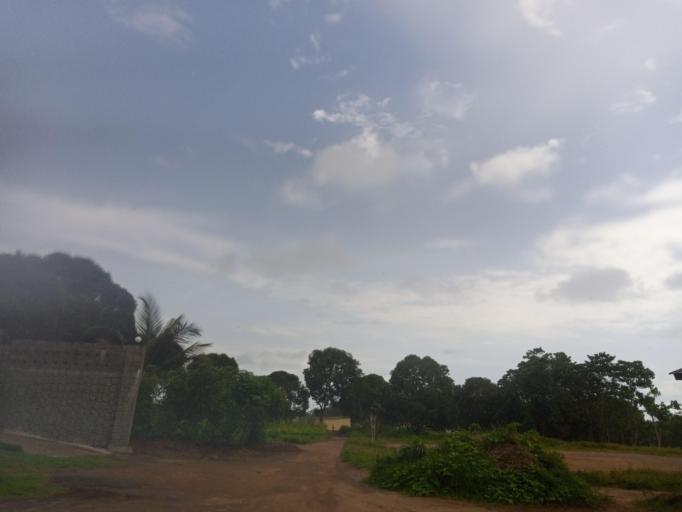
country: SL
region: Northern Province
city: Sawkta
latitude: 8.6316
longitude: -13.2052
